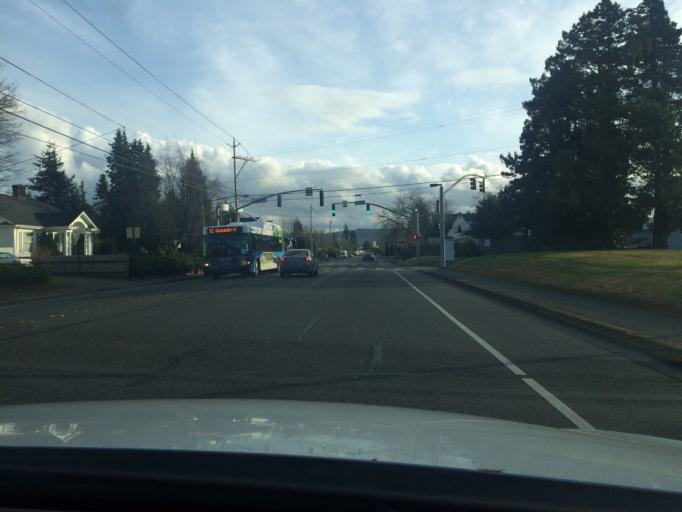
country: US
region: Washington
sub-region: Whatcom County
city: Bellingham
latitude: 48.7687
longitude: -122.4916
